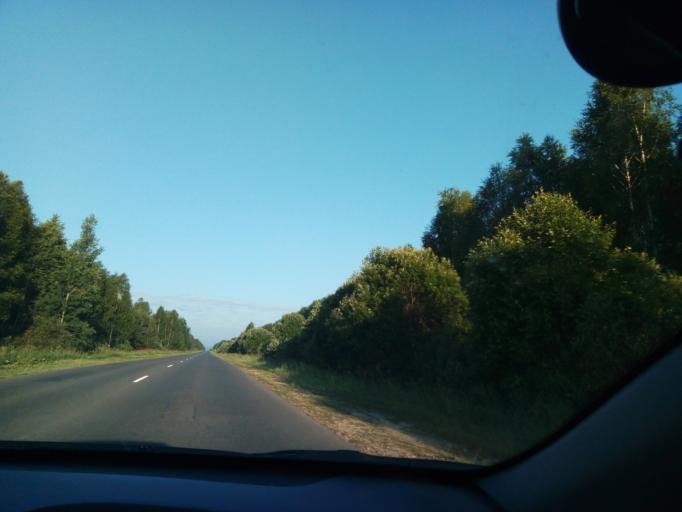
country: RU
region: Nizjnij Novgorod
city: Satis
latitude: 54.8986
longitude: 43.1249
